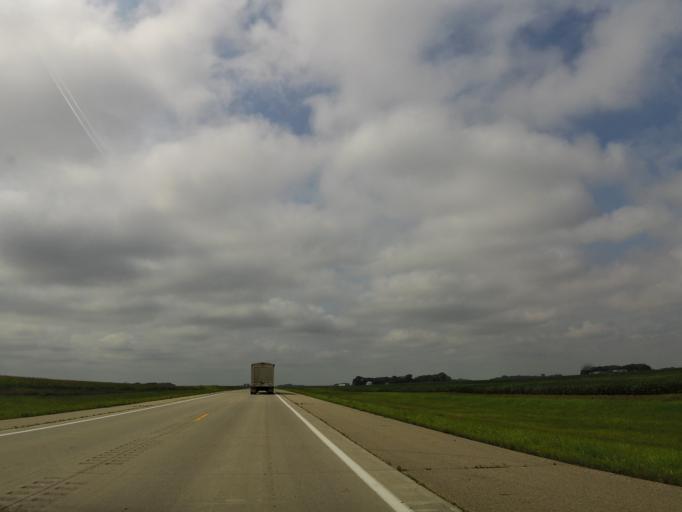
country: US
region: Minnesota
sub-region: Chippewa County
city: Montevideo
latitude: 44.9354
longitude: -95.8054
